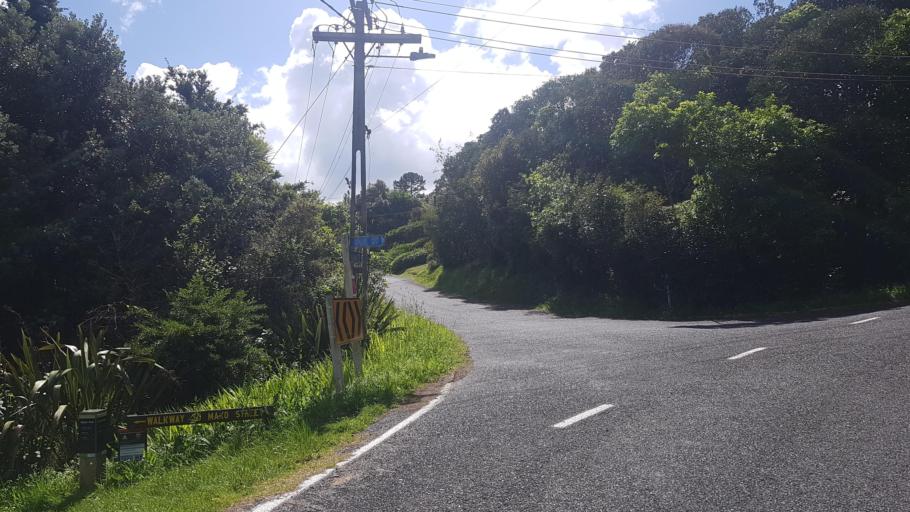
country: NZ
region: Auckland
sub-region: Auckland
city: Pakuranga
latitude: -36.7833
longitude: 175.0082
